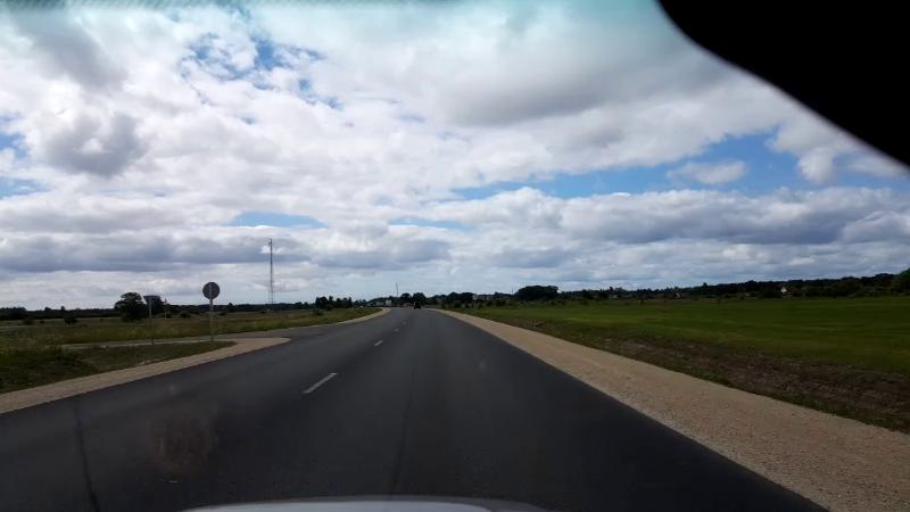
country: LV
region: Salacgrivas
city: Ainazi
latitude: 57.8647
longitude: 24.3711
